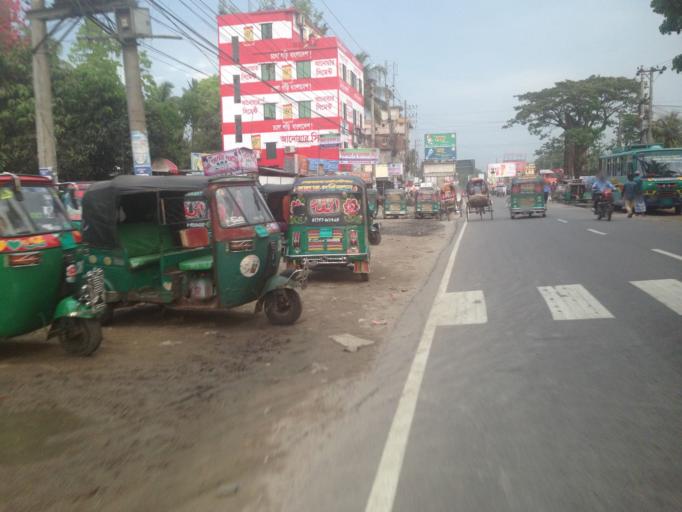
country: BD
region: Chittagong
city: Lakshmipur
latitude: 22.9450
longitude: 90.8265
